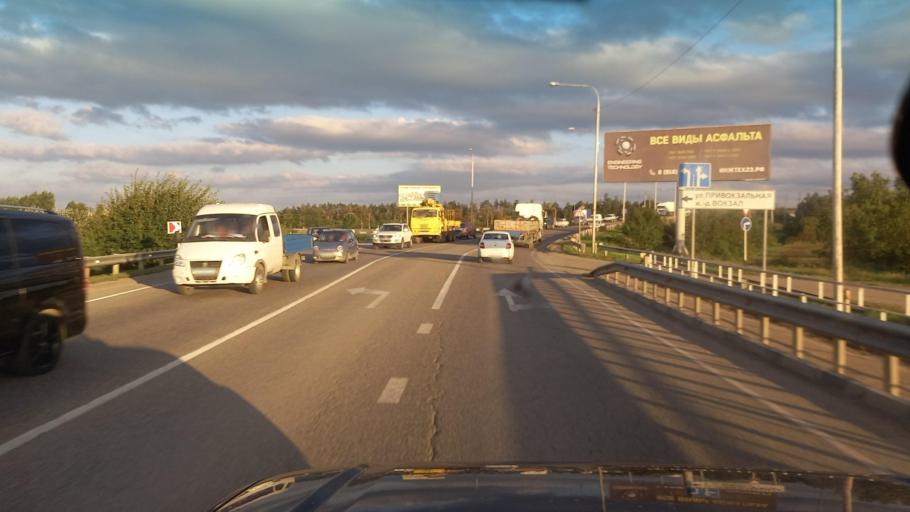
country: RU
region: Krasnodarskiy
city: Krymsk
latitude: 44.9053
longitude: 37.9772
